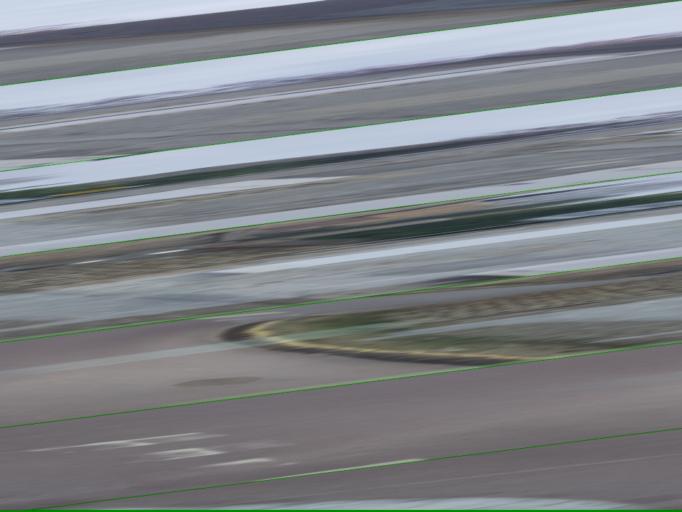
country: FR
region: Ile-de-France
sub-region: Departement des Yvelines
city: Houdan
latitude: 48.8315
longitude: 1.6087
